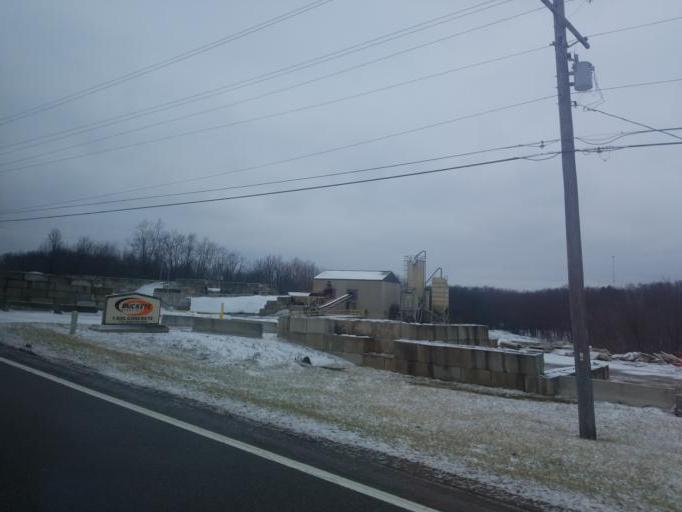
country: US
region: Ohio
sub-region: Licking County
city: Johnstown
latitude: 40.1659
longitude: -82.6987
